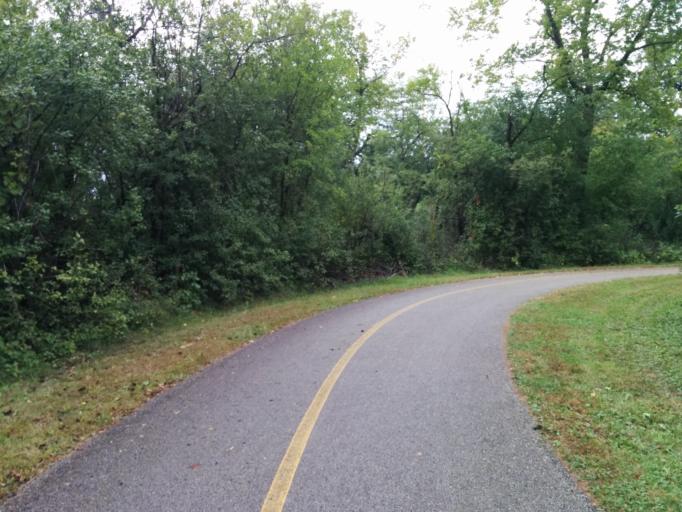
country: US
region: Illinois
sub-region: Cook County
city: Northfield
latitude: 42.1155
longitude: -87.7767
